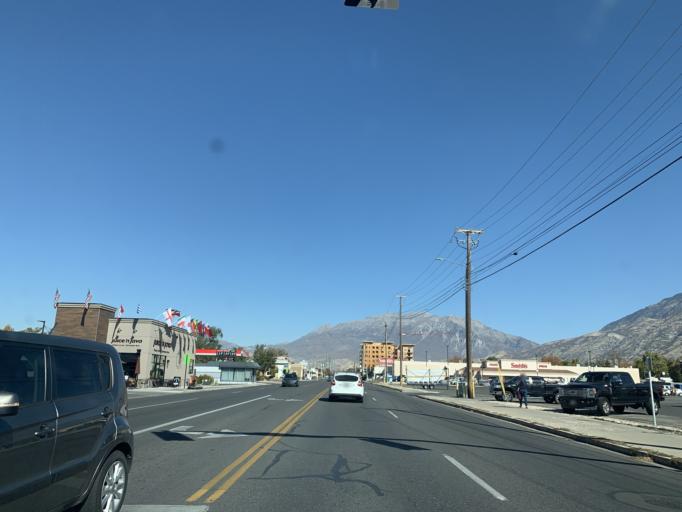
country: US
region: Utah
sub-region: Utah County
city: Provo
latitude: 40.2366
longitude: -111.6622
